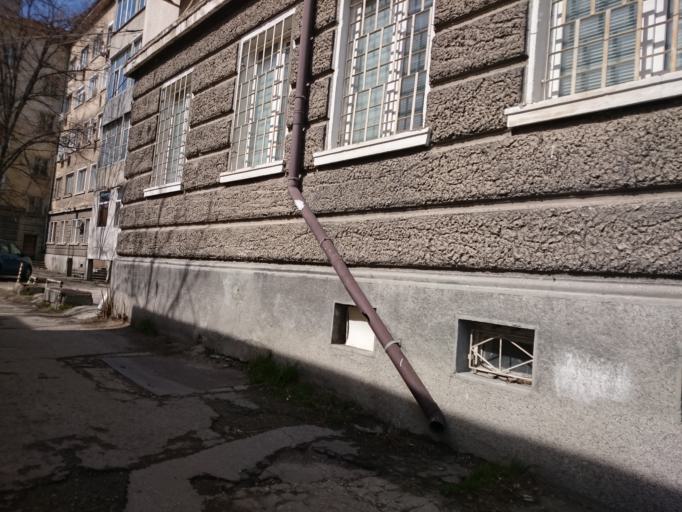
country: BG
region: Varna
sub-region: Obshtina Varna
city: Varna
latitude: 43.2053
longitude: 27.9066
